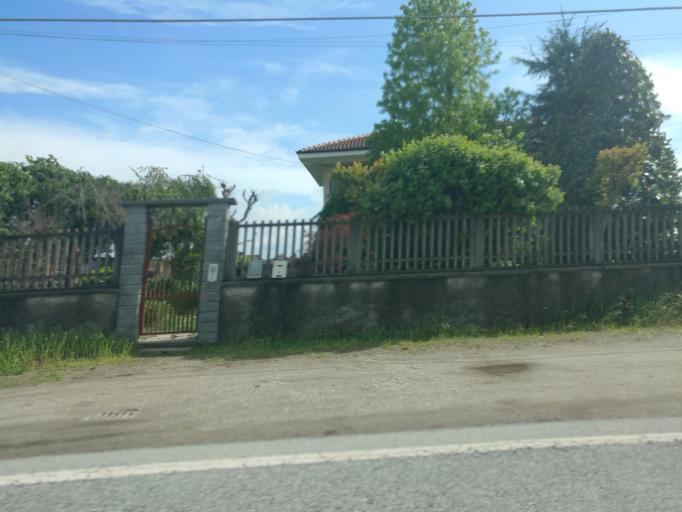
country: IT
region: Piedmont
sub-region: Provincia di Torino
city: Pancalieri
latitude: 44.8357
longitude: 7.5800
